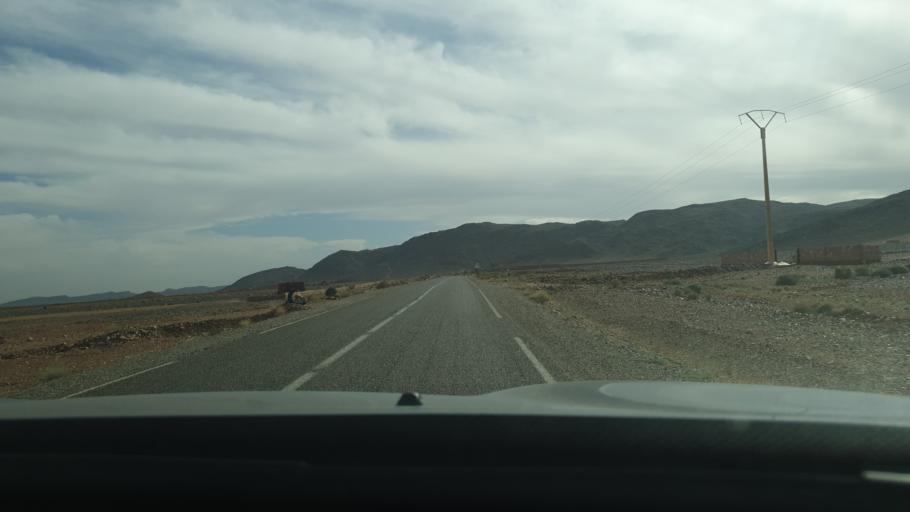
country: MA
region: Meknes-Tafilalet
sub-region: Errachidia
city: Fezna
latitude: 31.5311
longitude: -4.6397
